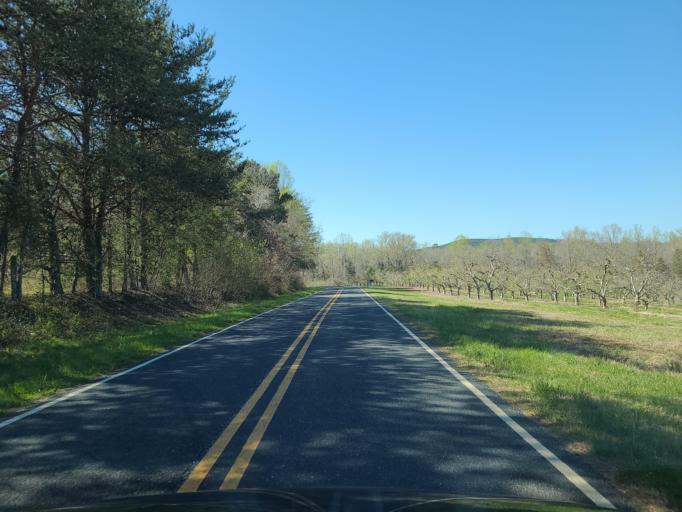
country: US
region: North Carolina
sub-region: Gaston County
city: Cherryville
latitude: 35.5258
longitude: -81.5044
